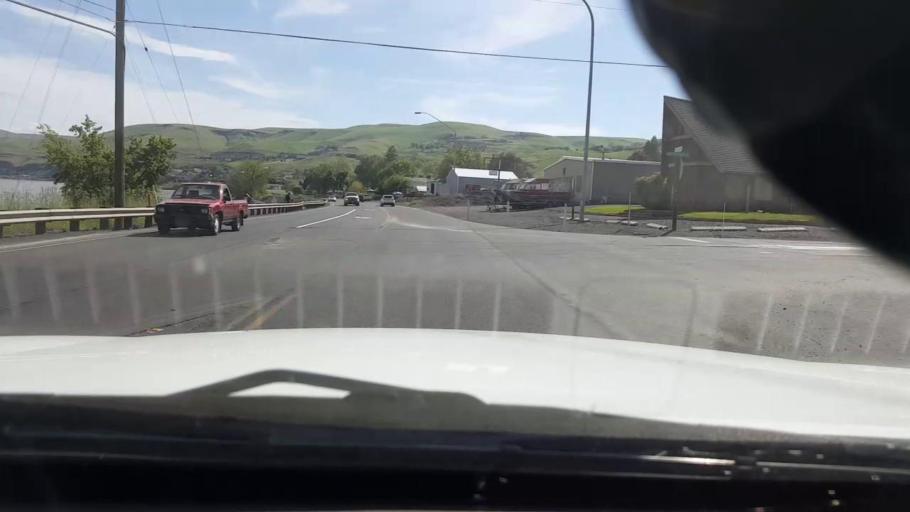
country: US
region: Washington
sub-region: Asotin County
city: Clarkston Heights-Vineland
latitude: 46.3685
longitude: -117.0630
